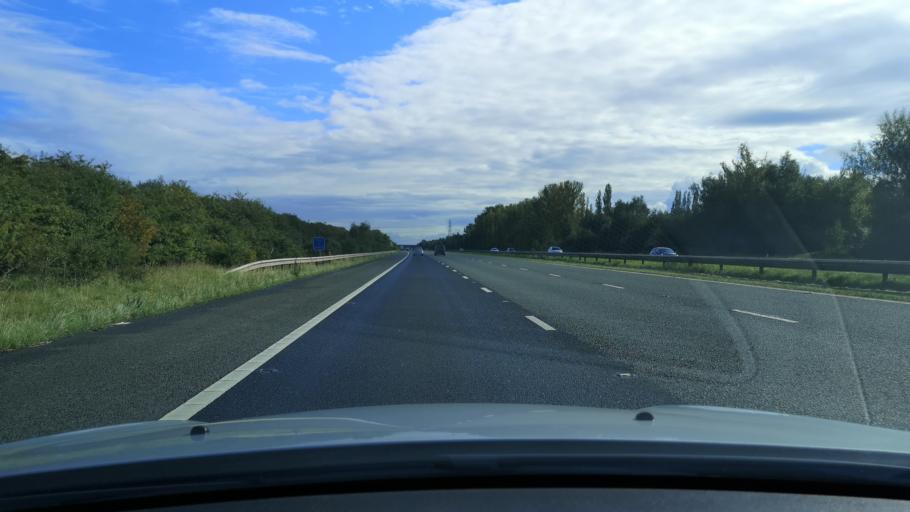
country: GB
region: England
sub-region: East Riding of Yorkshire
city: Pollington
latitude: 53.6828
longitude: -1.0706
